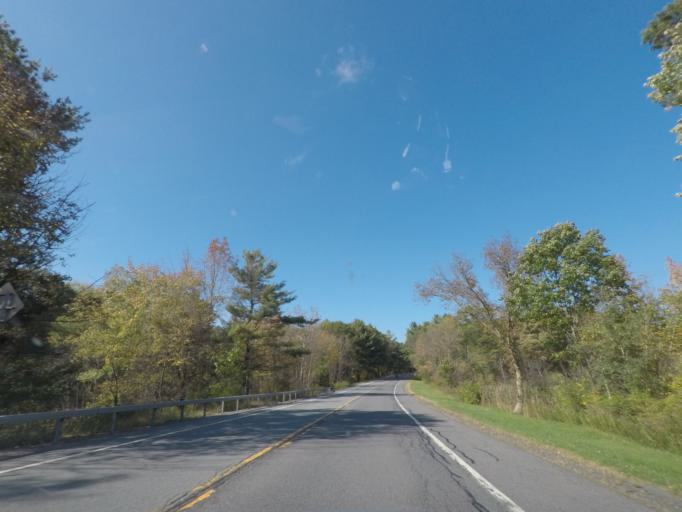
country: US
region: New York
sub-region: Rensselaer County
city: Averill Park
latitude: 42.6410
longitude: -73.5462
